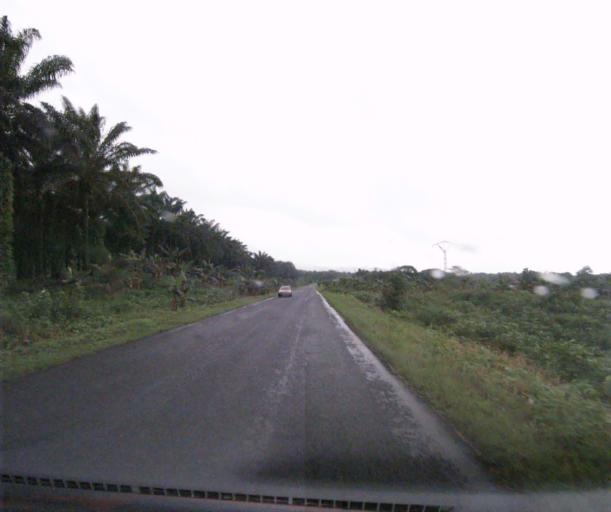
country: CM
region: South-West Province
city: Idenao
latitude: 4.1965
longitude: 9.0026
